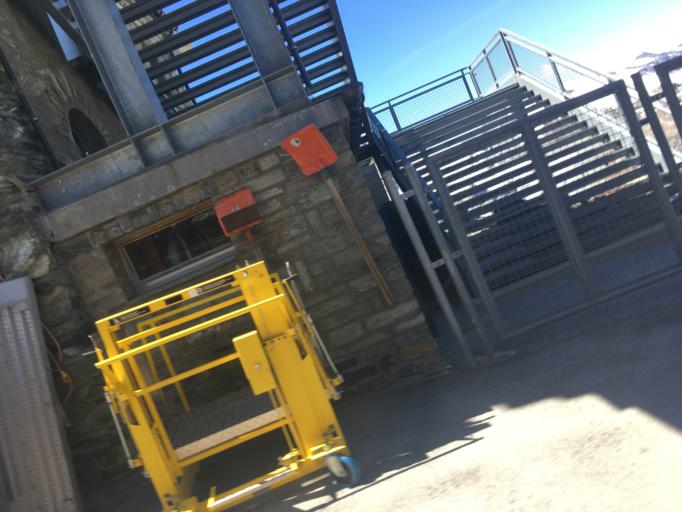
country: CH
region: Valais
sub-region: Visp District
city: Zermatt
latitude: 45.9835
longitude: 7.7820
